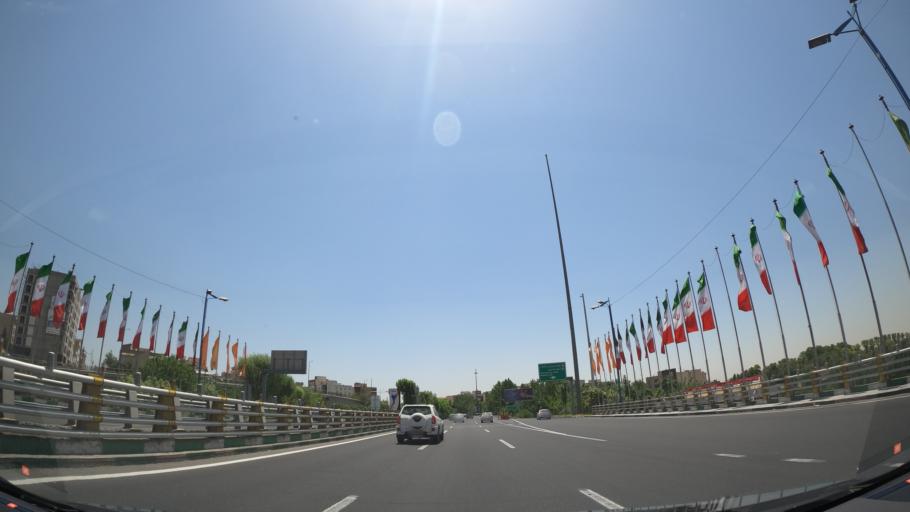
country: IR
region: Tehran
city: Tajrish
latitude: 35.7767
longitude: 51.3902
